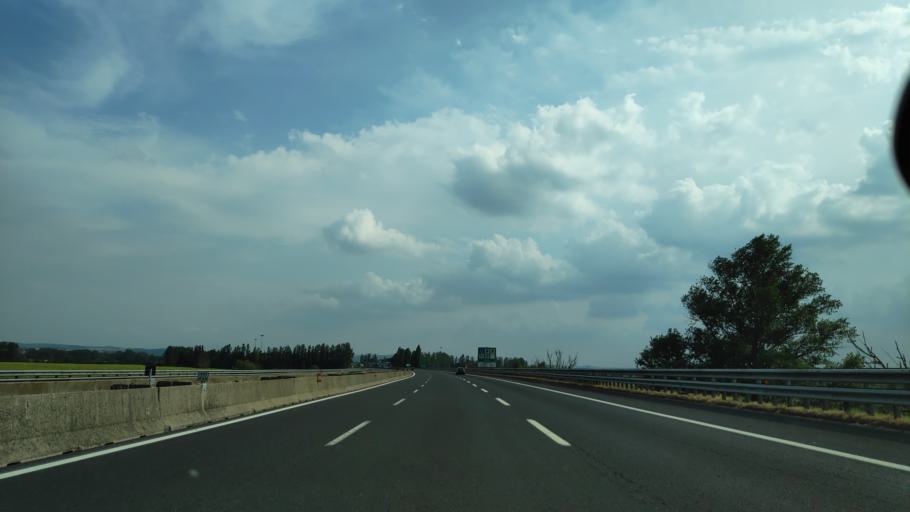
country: IT
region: Latium
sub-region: Citta metropolitana di Roma Capitale
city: Bivio di Capanelle
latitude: 42.1310
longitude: 12.6172
